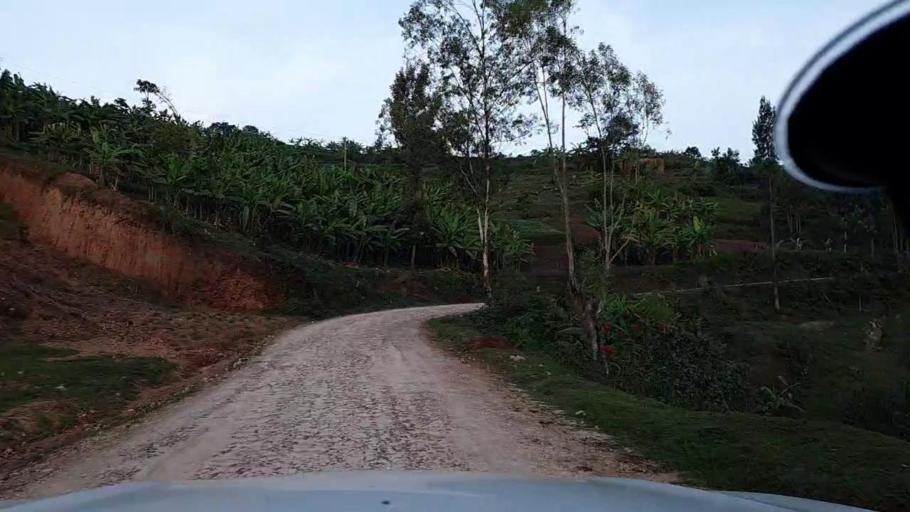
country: RW
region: Southern Province
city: Nyanza
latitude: -2.2119
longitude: 29.6328
